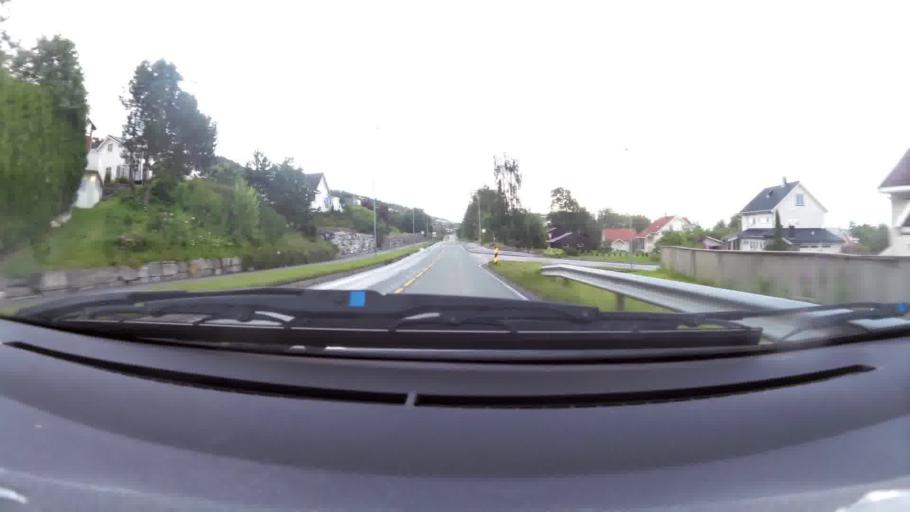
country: NO
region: More og Romsdal
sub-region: Molde
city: Molde
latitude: 62.7457
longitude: 7.2079
